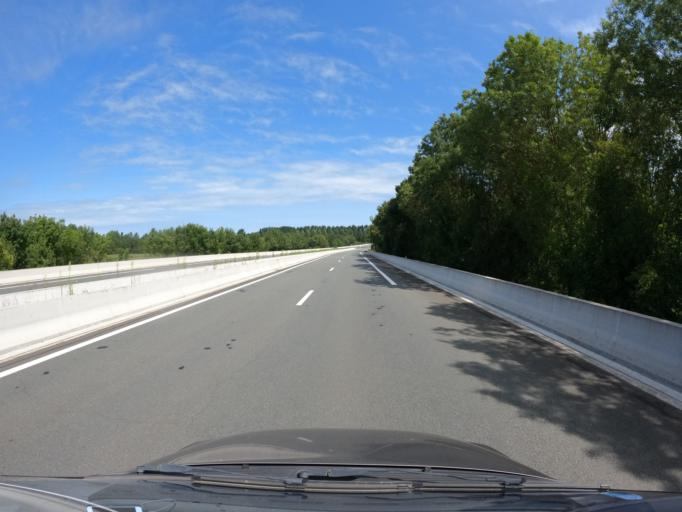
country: FR
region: Poitou-Charentes
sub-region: Departement des Deux-Sevres
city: Frontenay-Rohan-Rohan
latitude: 46.2313
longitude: -0.5874
